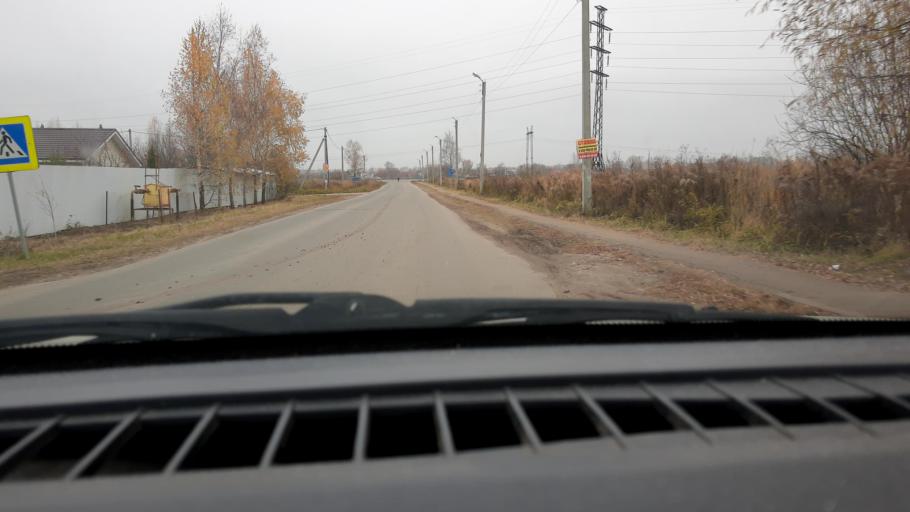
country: RU
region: Nizjnij Novgorod
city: Afonino
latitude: 56.2063
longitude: 44.0970
